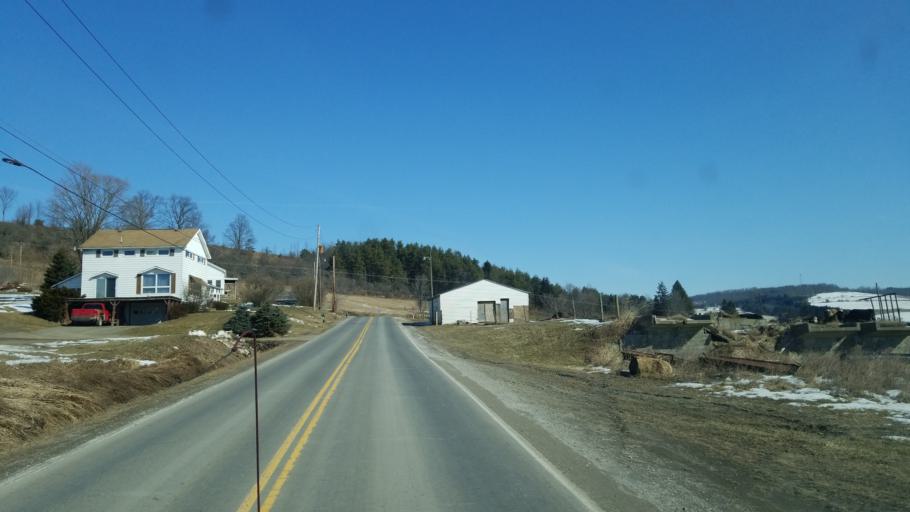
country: US
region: Pennsylvania
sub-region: Tioga County
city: Elkland
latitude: 42.0781
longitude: -77.4177
